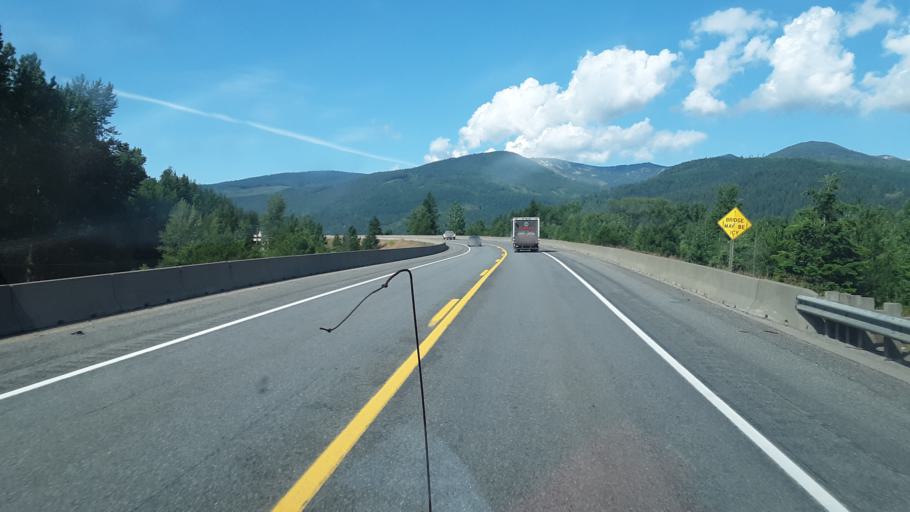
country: US
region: Idaho
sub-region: Bonner County
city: Ponderay
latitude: 48.4151
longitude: -116.5139
